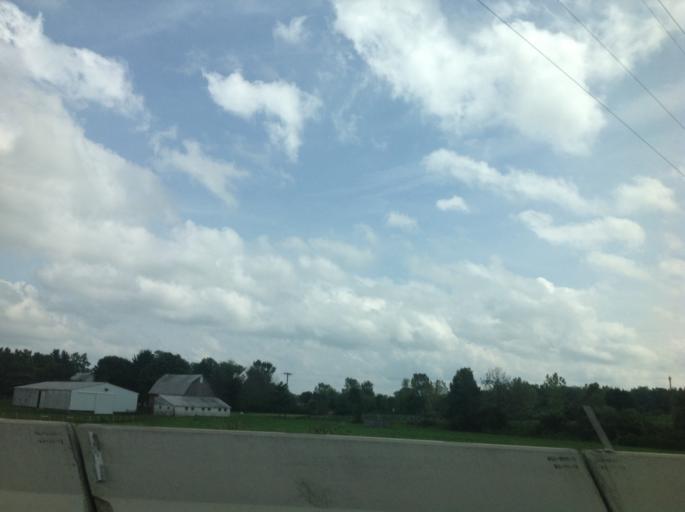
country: US
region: Ohio
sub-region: Morrow County
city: Mount Gilead
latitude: 40.4617
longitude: -82.7698
